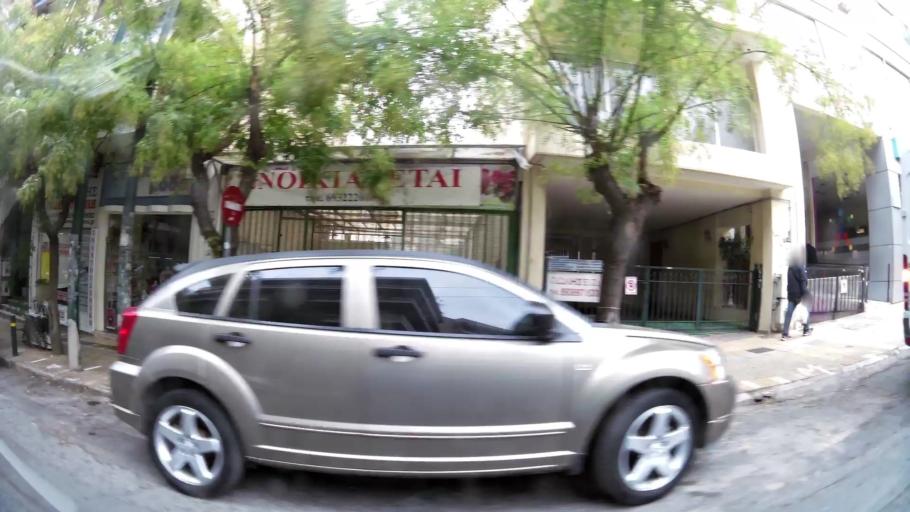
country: GR
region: Attica
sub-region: Nomarchia Athinas
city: Ymittos
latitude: 37.9605
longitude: 23.7415
